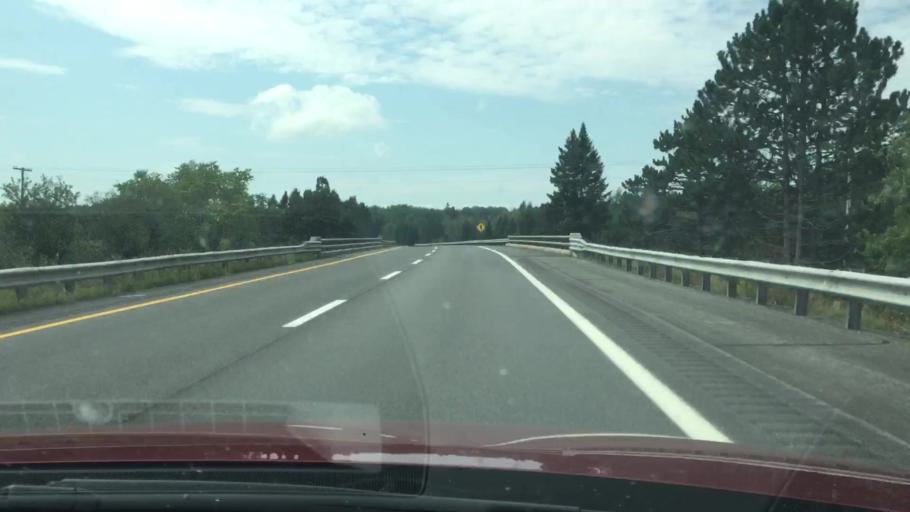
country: US
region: Maine
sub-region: Aroostook County
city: Hodgdon
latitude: 46.1108
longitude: -68.1598
